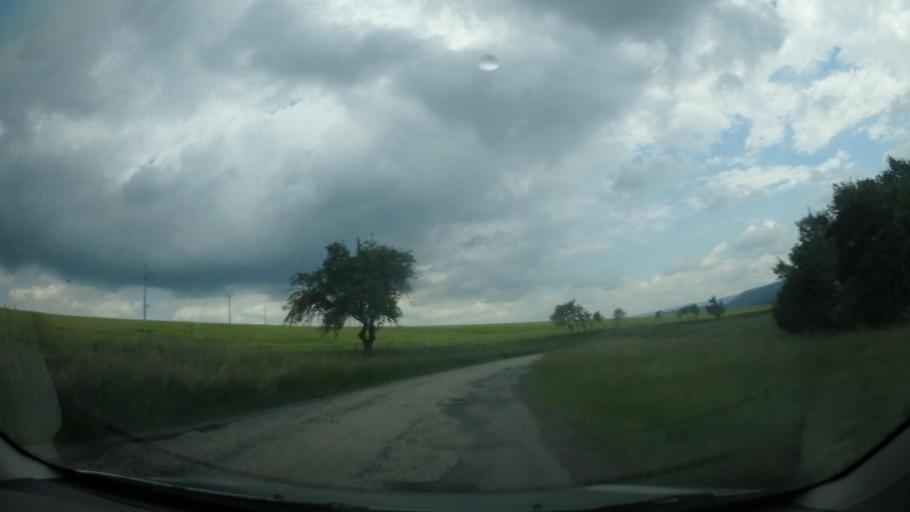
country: CZ
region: South Moravian
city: Boritov
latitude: 49.4590
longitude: 16.5962
